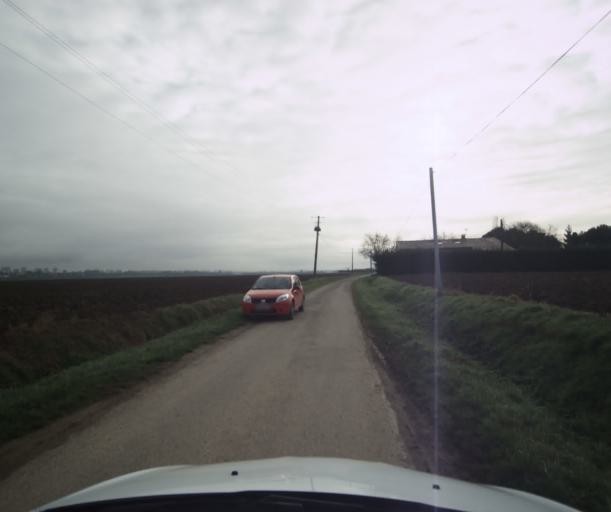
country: FR
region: Midi-Pyrenees
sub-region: Departement du Tarn-et-Garonne
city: Castelsarrasin
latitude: 44.0246
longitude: 1.1239
